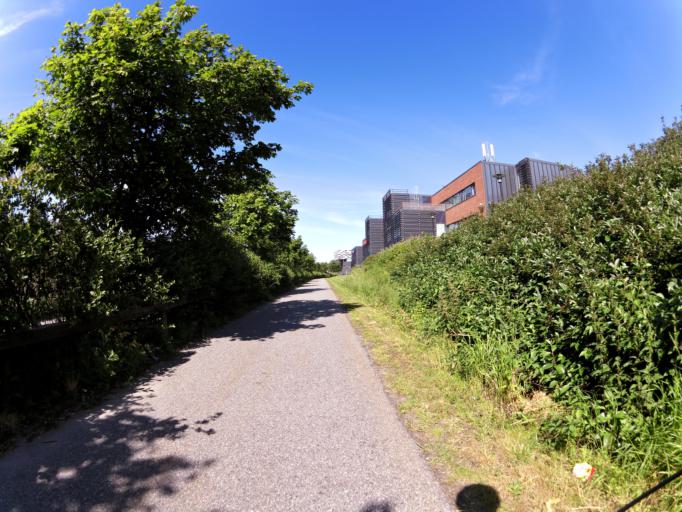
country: NO
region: Ostfold
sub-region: Fredrikstad
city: Fredrikstad
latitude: 59.2219
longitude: 10.9508
